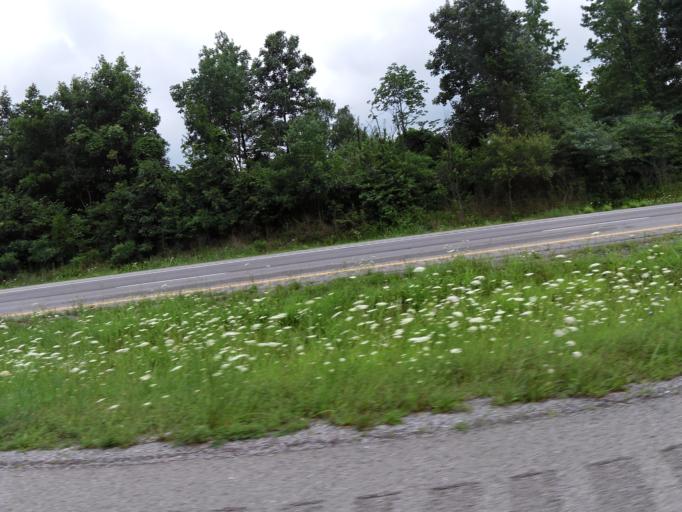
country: US
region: Kentucky
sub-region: Muhlenberg County
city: Central City
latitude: 37.3216
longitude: -87.0305
